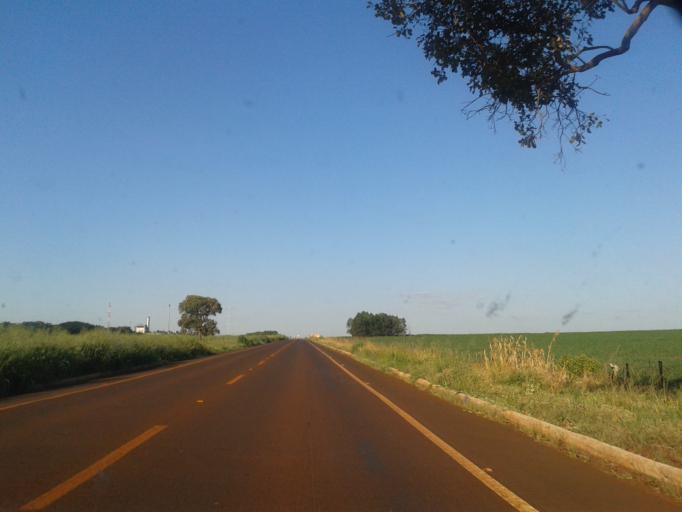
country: BR
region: Minas Gerais
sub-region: Capinopolis
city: Capinopolis
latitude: -18.7061
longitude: -49.6914
